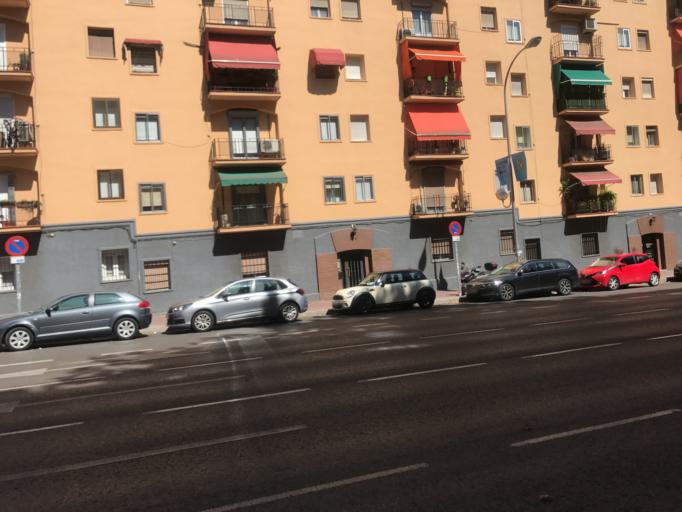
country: ES
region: Madrid
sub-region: Provincia de Madrid
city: Arganzuela
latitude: 40.3998
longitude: -3.6939
